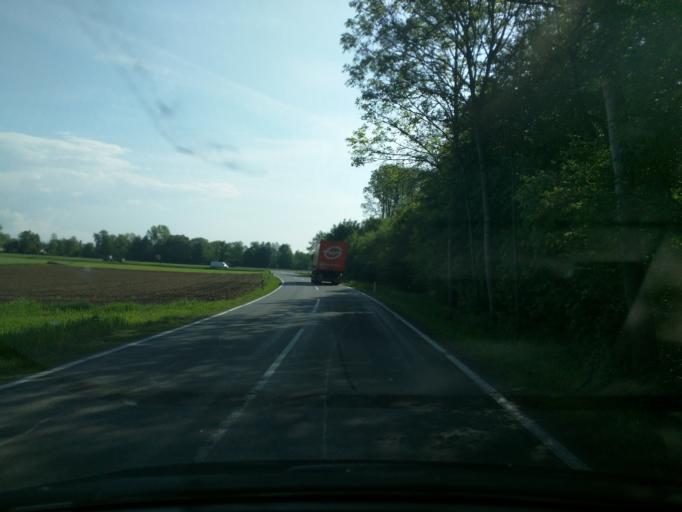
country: AT
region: Lower Austria
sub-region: Politischer Bezirk Amstetten
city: Euratsfeld
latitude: 48.0762
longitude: 14.8964
